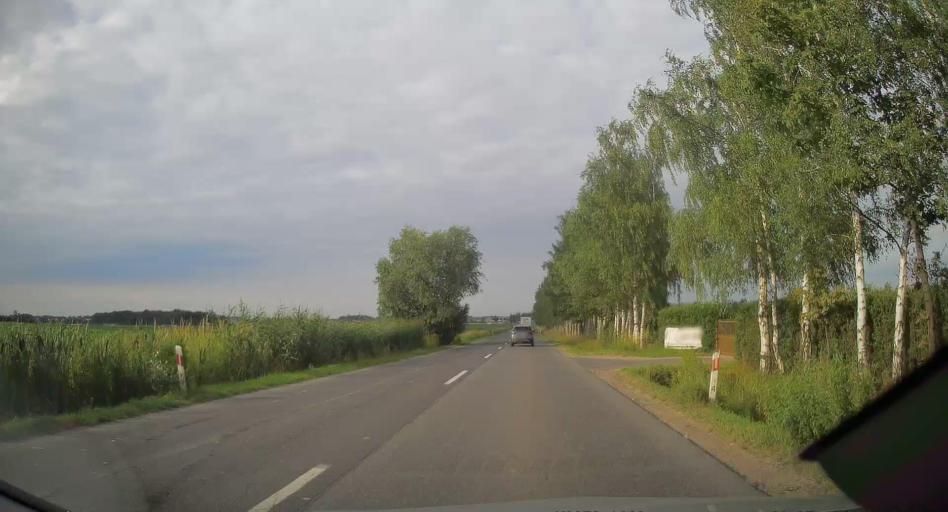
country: PL
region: Lower Silesian Voivodeship
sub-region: Powiat wroclawski
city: Tyniec Maly
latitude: 51.0310
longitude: 16.8886
